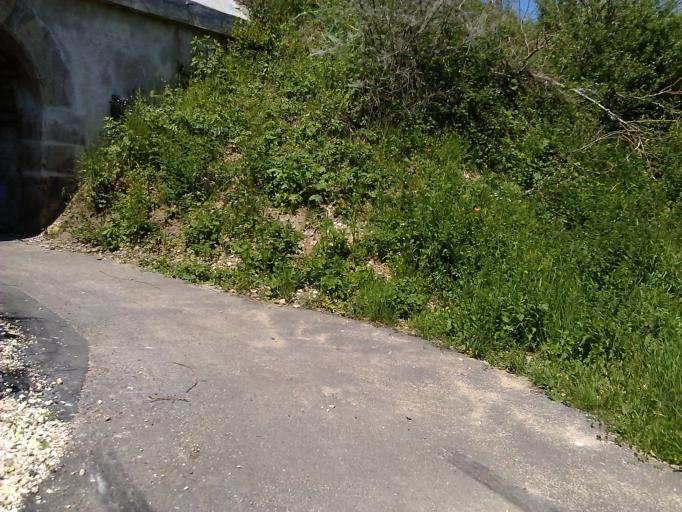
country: FR
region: Centre
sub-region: Departement de l'Indre
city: Saint-Marcel
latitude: 46.6095
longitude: 1.4974
